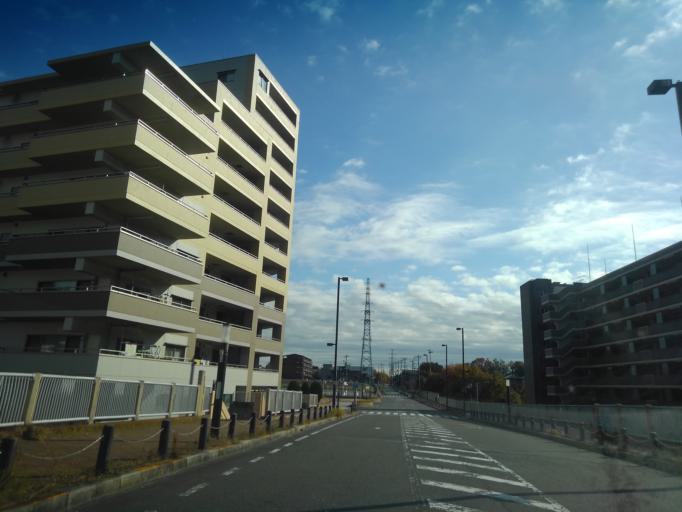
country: JP
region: Tokyo
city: Hachioji
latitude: 35.6021
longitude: 139.3655
